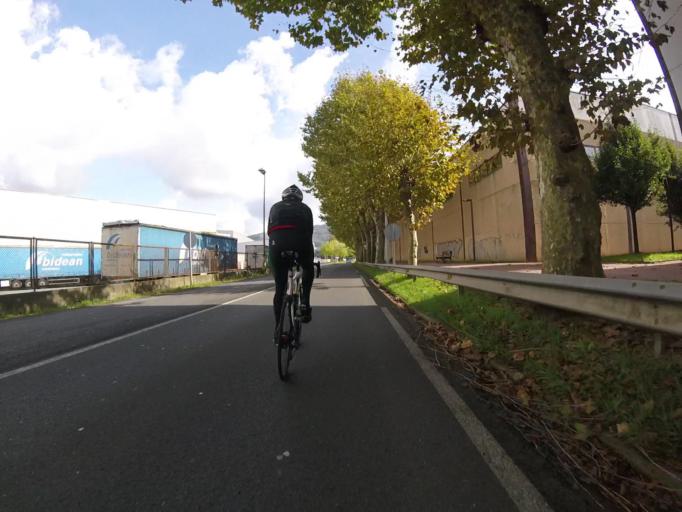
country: ES
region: Basque Country
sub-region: Provincia de Guipuzcoa
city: Hernani
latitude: 43.2674
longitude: -1.9632
